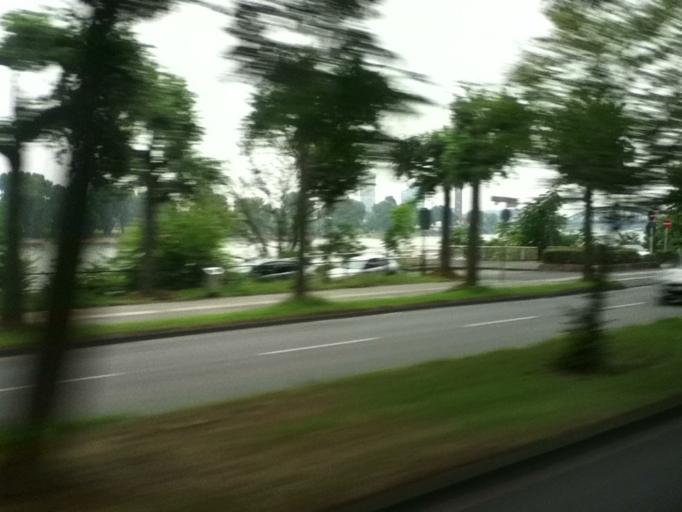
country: DE
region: North Rhine-Westphalia
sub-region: Regierungsbezirk Koln
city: Riehl
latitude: 50.9546
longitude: 6.9715
